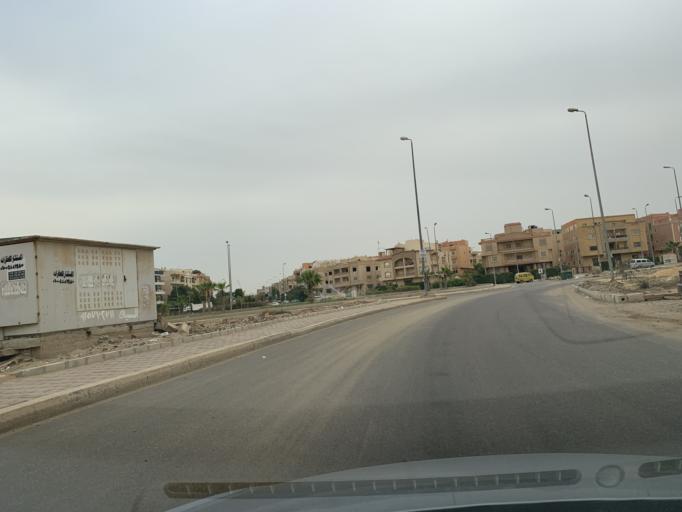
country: EG
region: Al Jizah
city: Awsim
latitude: 30.0318
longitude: 30.9795
